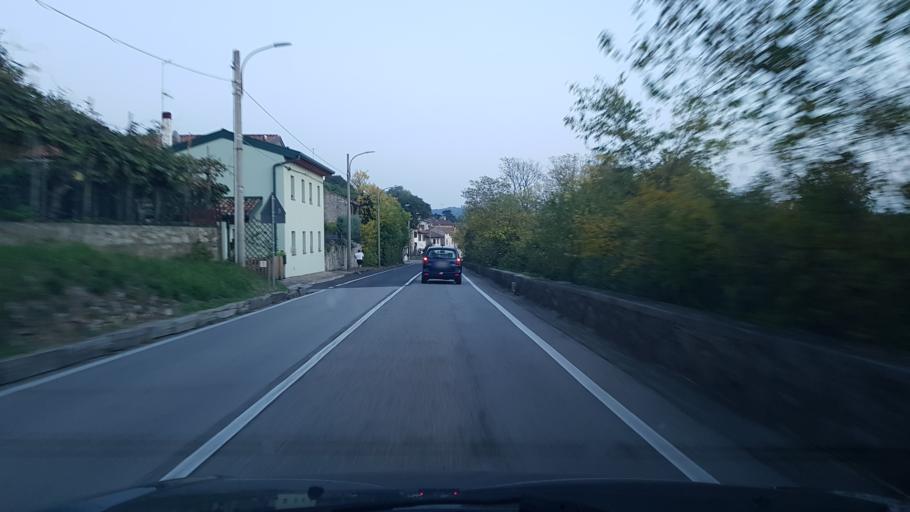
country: IT
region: Friuli Venezia Giulia
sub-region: Provincia di Gorizia
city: Ronchi dei Legionari
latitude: 45.8270
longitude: 13.5216
